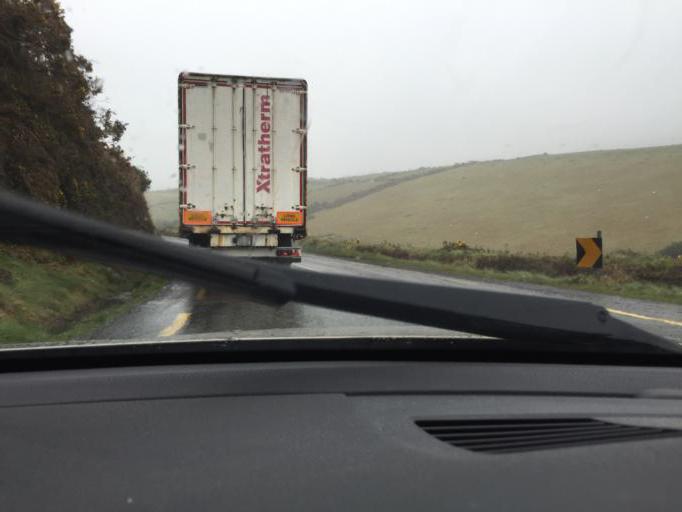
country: IE
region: Munster
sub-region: Ciarrai
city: Dingle
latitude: 52.1448
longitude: -10.0861
